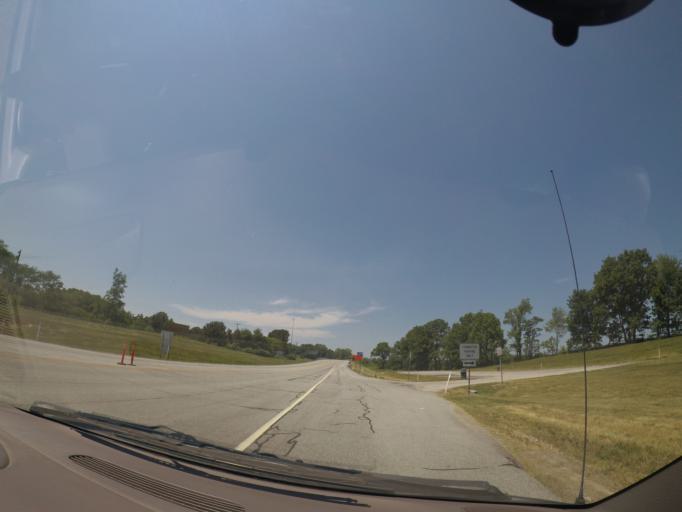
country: US
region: Indiana
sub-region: LaPorte County
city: LaPorte
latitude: 41.6678
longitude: -86.7358
